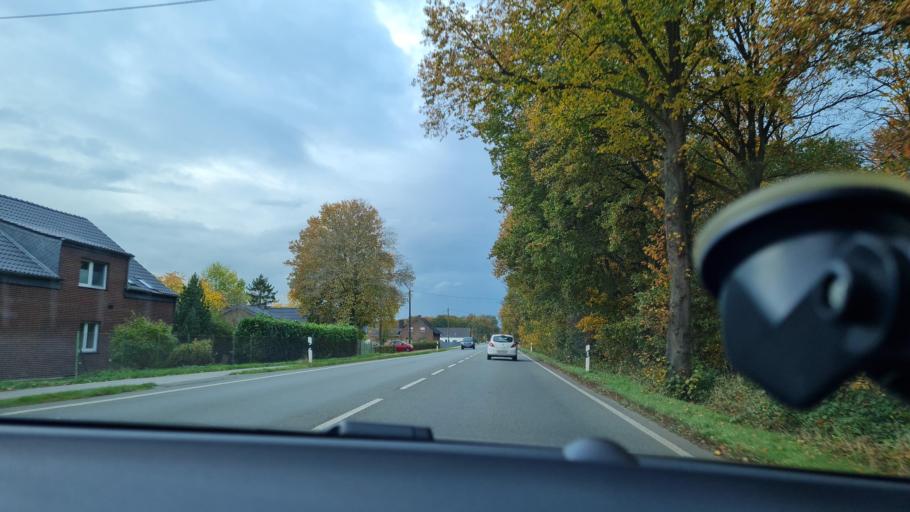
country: DE
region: North Rhine-Westphalia
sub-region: Regierungsbezirk Dusseldorf
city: Voerde
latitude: 51.6186
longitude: 6.6806
